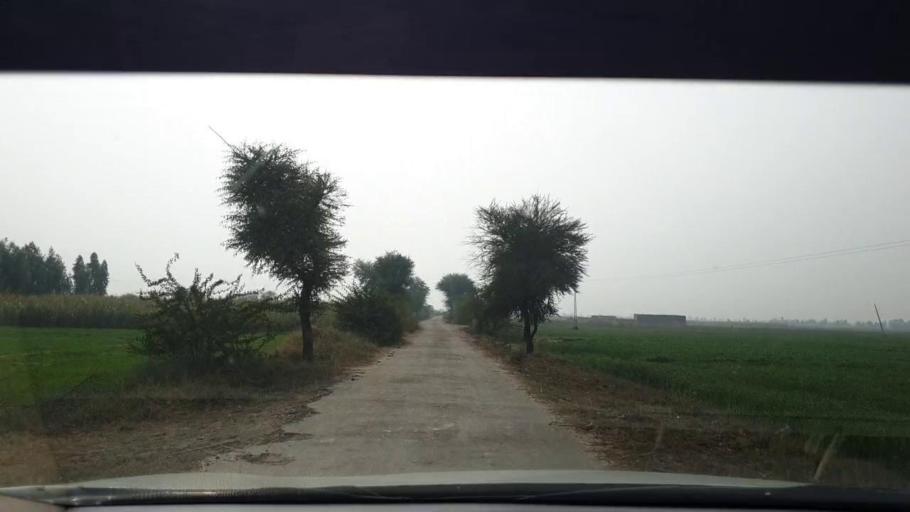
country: PK
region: Sindh
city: Berani
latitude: 25.8434
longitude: 68.8271
